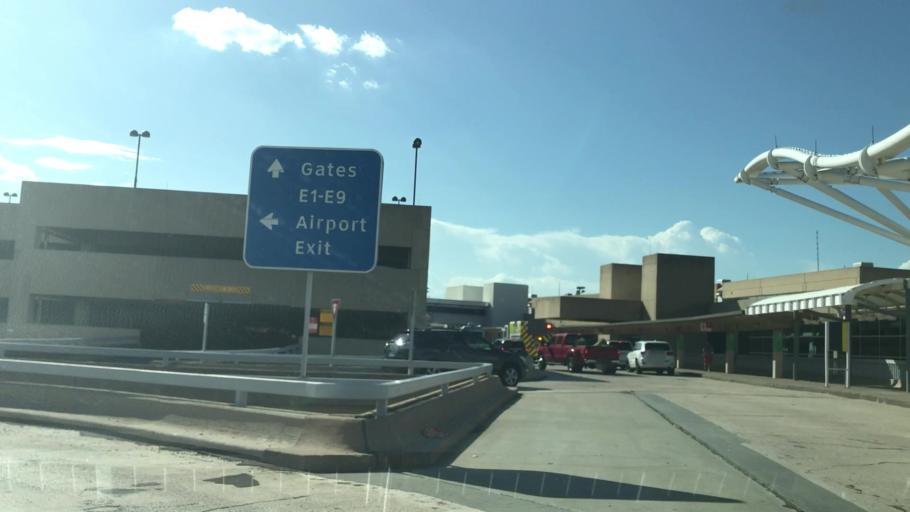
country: US
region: Texas
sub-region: Tarrant County
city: Grapevine
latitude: 32.8914
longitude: -97.0366
